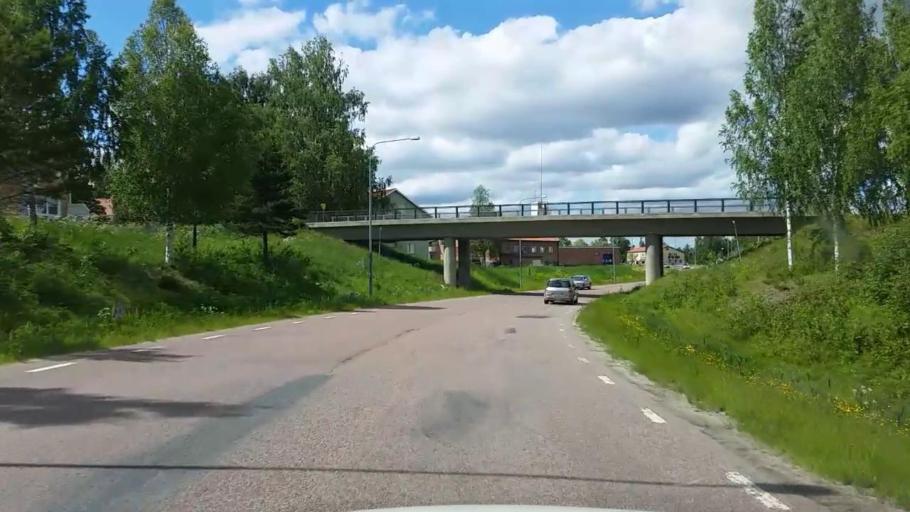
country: SE
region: Gaevleborg
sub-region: Ovanakers Kommun
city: Alfta
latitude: 61.3425
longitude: 16.0644
